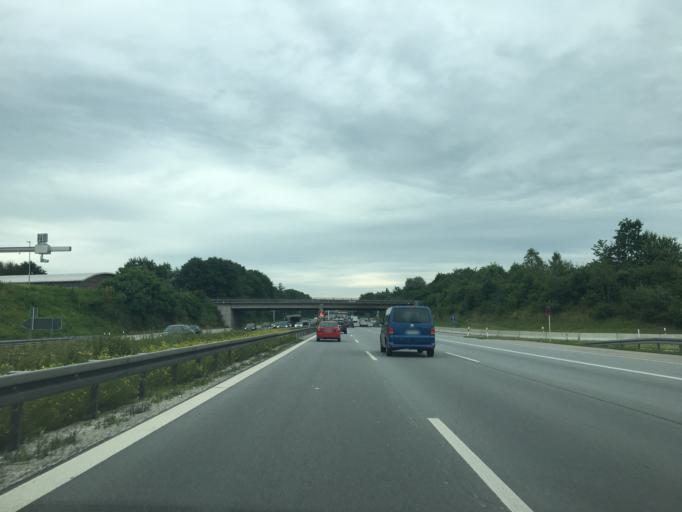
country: DE
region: Bavaria
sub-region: Upper Bavaria
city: Allershausen
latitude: 48.4275
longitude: 11.5895
